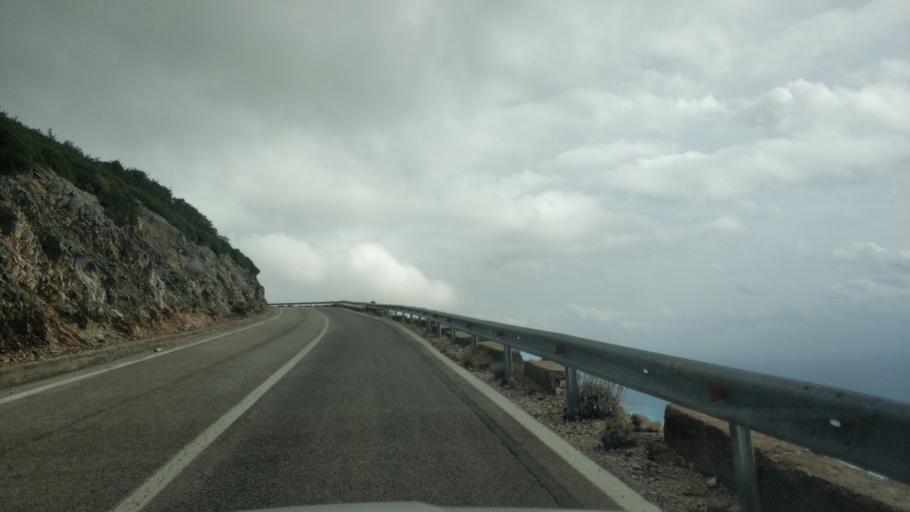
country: AL
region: Vlore
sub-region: Rrethi i Vlores
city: Vranisht
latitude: 40.1843
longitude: 19.5966
